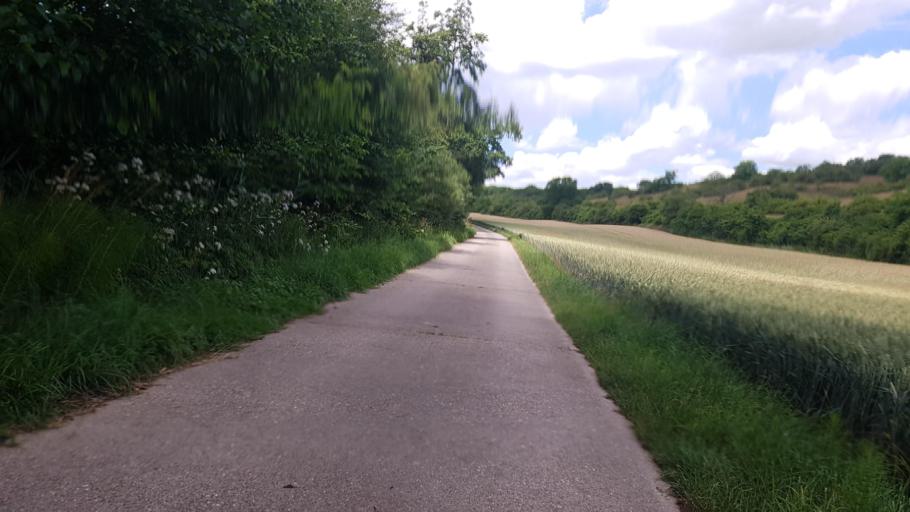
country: DE
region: Baden-Wuerttemberg
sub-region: Karlsruhe Region
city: Zaisenhausen
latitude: 49.1660
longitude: 8.7890
